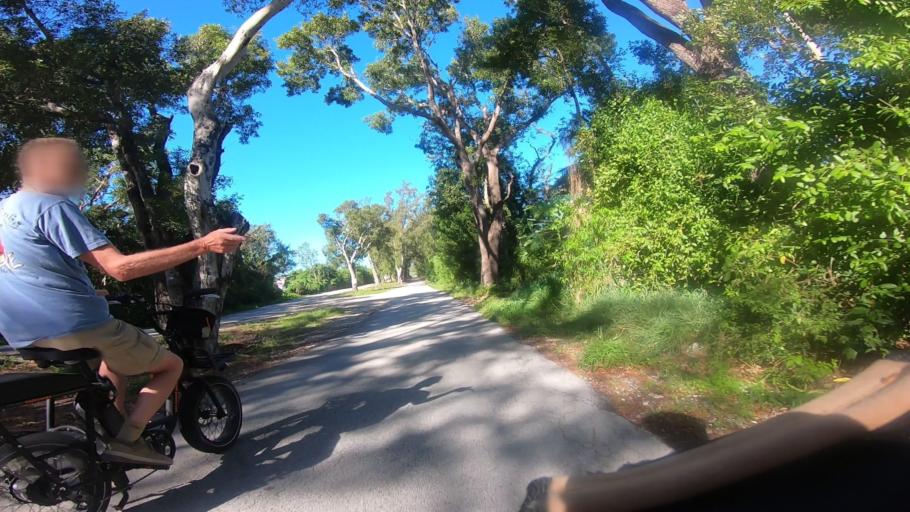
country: US
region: Florida
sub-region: Monroe County
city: Key Largo
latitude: 25.1118
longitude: -80.4270
